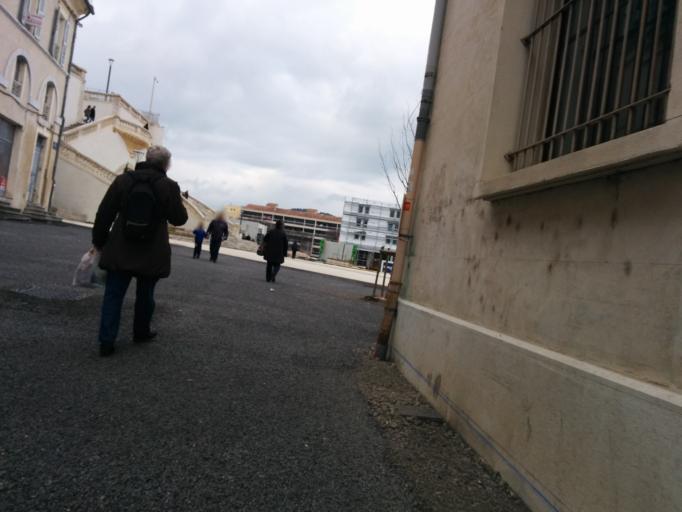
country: FR
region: Languedoc-Roussillon
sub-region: Departement du Gard
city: Ales
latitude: 44.1261
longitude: 4.0784
